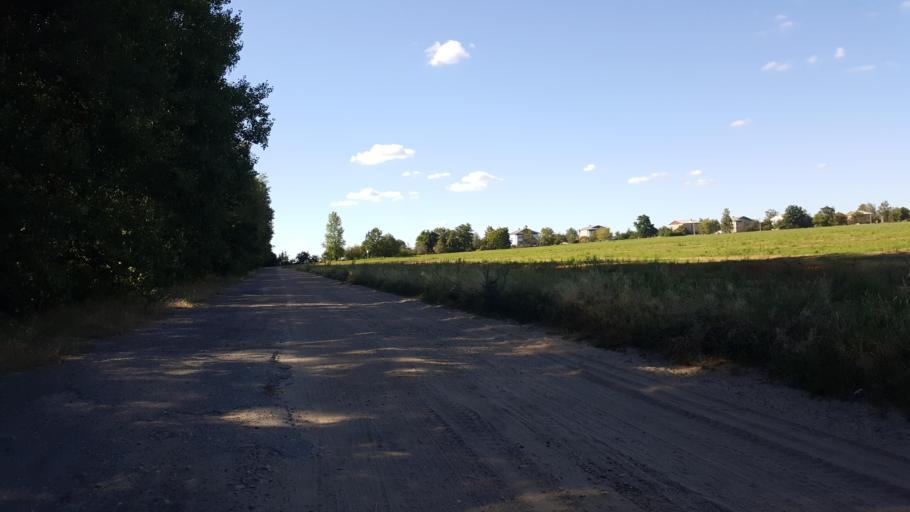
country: BY
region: Brest
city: Vysokaye
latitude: 52.3362
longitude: 23.5485
